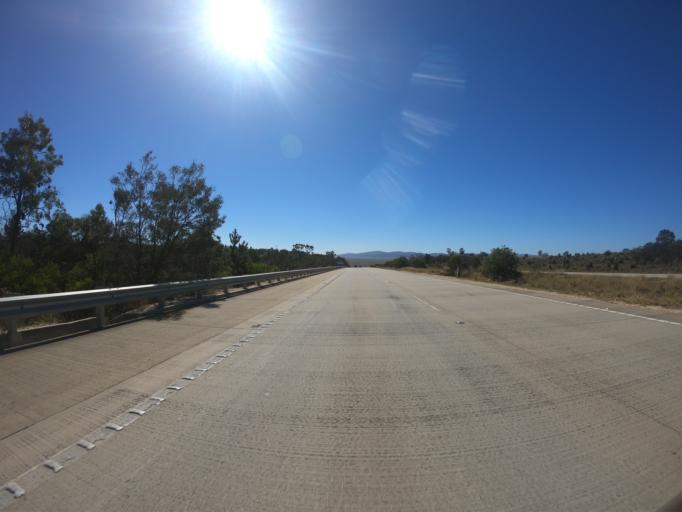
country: AU
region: New South Wales
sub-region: Yass Valley
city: Gundaroo
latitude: -35.1047
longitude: 149.3723
